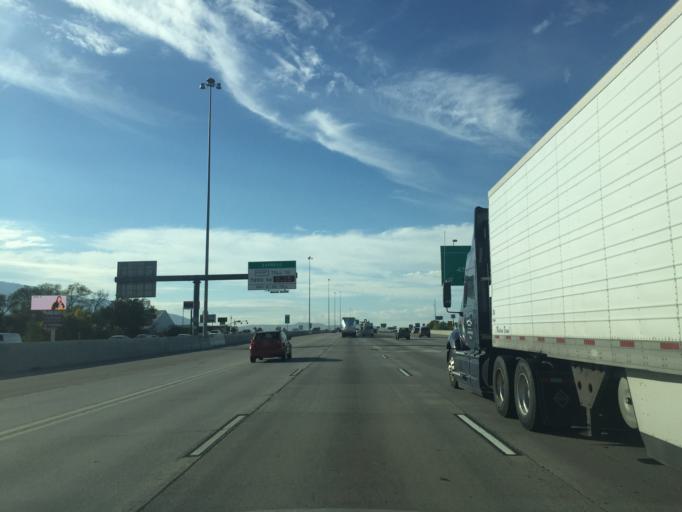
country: US
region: Utah
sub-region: Salt Lake County
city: Centerfield
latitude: 40.6802
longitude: -111.9023
